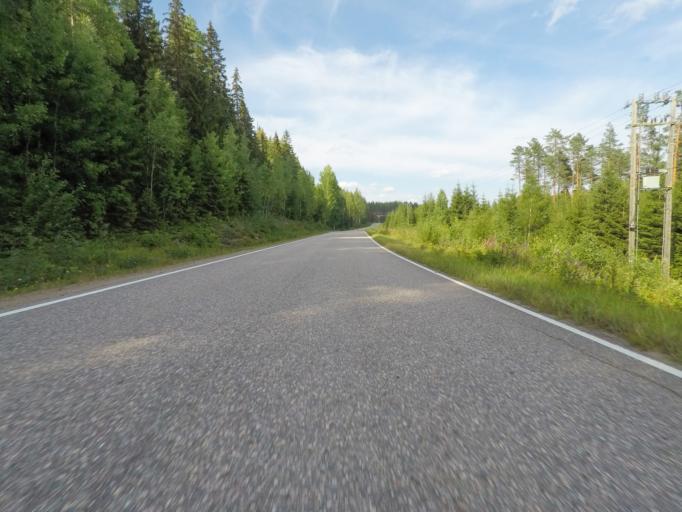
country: FI
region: Southern Savonia
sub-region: Savonlinna
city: Sulkava
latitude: 61.7267
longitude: 28.2047
